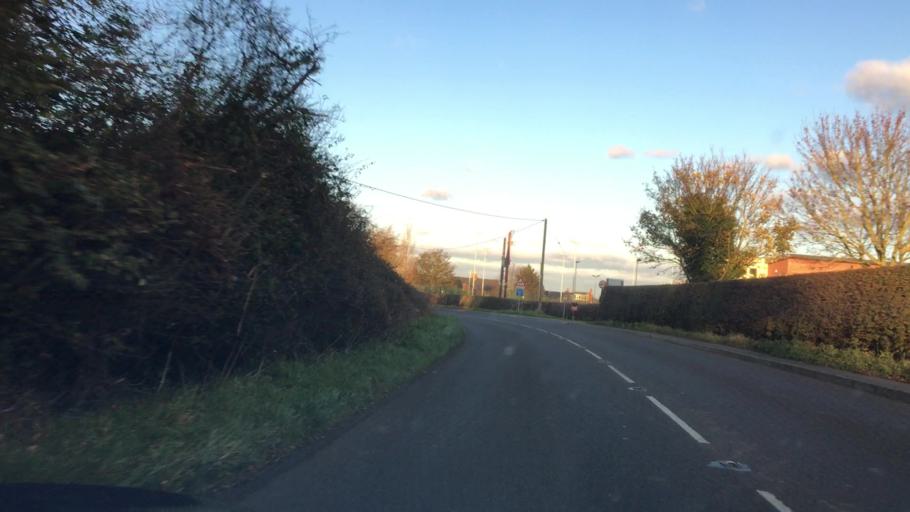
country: GB
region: England
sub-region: Derbyshire
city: Melbourne
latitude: 52.8227
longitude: -1.4402
